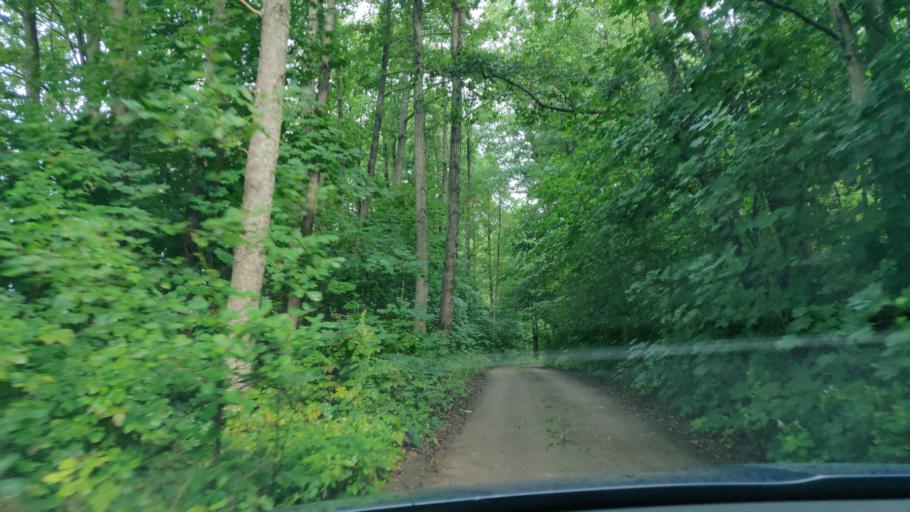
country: LT
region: Vilnius County
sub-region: Trakai
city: Rudiskes
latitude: 54.6087
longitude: 24.8377
